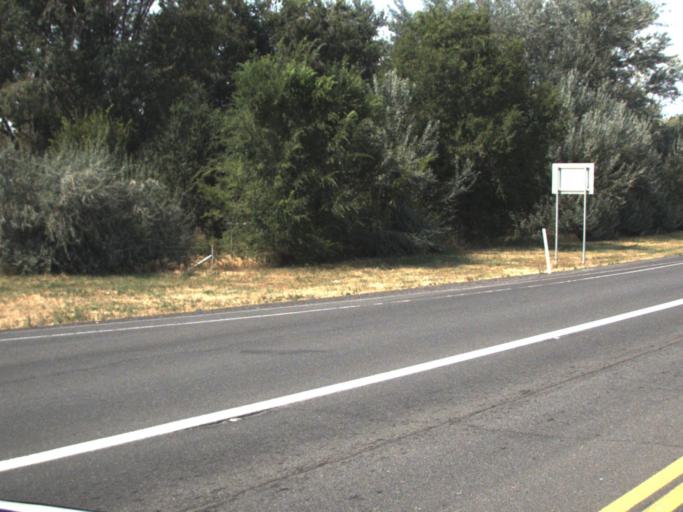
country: US
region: Washington
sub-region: Yakima County
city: Terrace Heights
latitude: 46.5571
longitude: -120.3938
